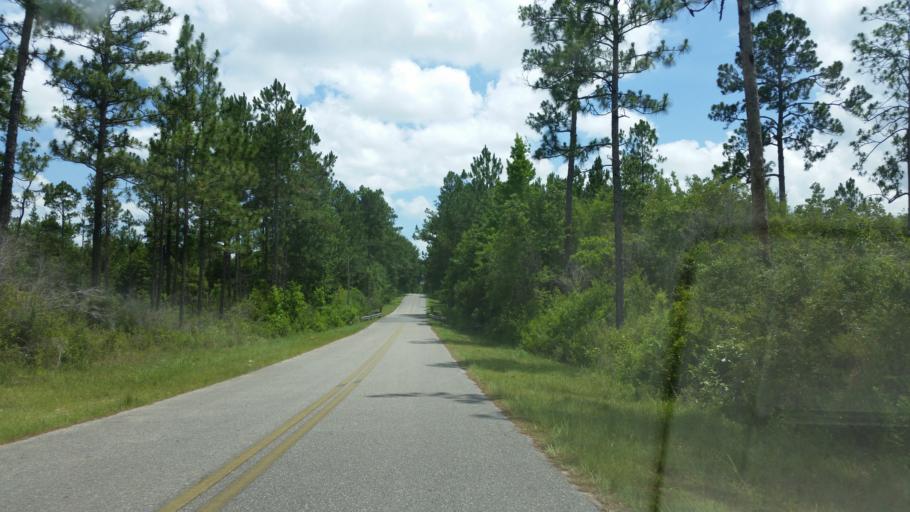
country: US
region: Florida
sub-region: Santa Rosa County
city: Point Baker
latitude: 30.7313
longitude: -86.8750
